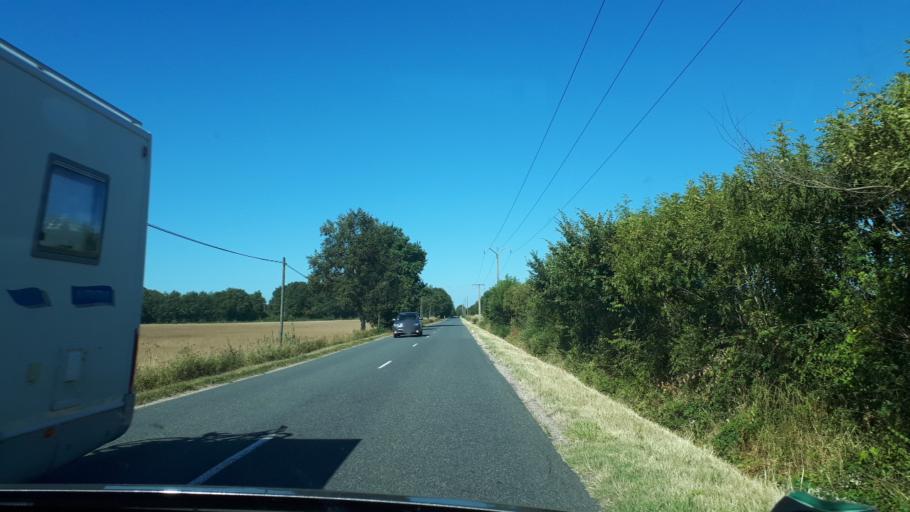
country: FR
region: Centre
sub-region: Departement du Loiret
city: Coullons
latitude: 47.6188
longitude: 2.5297
